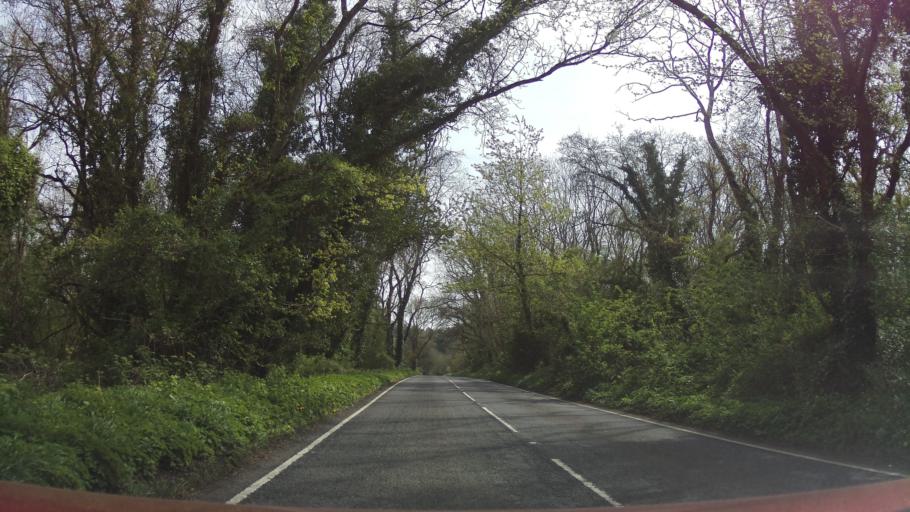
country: GB
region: England
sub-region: Somerset
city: Street
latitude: 51.1075
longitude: -2.7427
